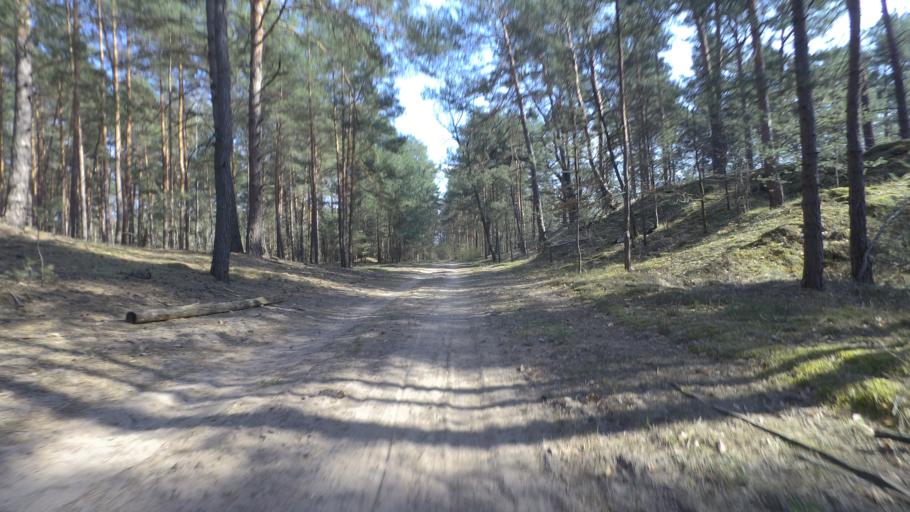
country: DE
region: Brandenburg
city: Mittenwalde
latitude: 52.1809
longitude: 13.5550
